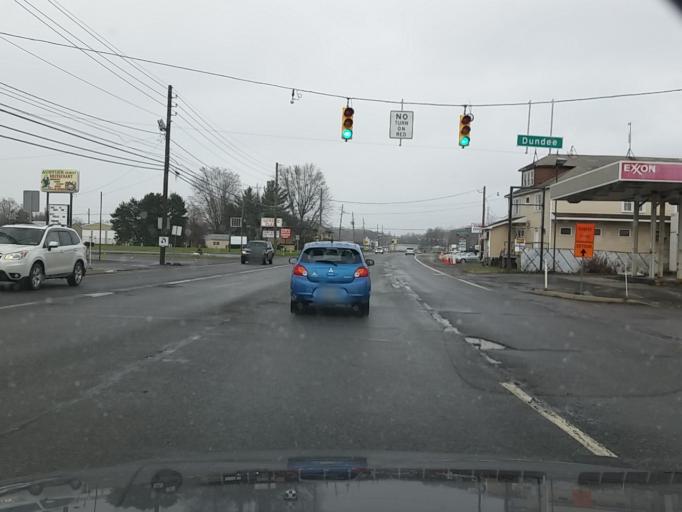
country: US
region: Pennsylvania
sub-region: Luzerne County
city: Nanticoke
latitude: 41.2096
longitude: -75.9750
